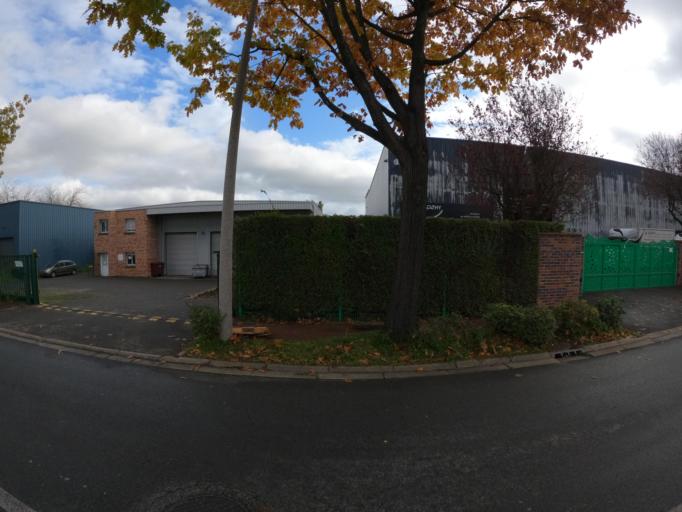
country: FR
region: Ile-de-France
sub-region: Departement de Seine-et-Marne
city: Chelles
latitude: 48.8909
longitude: 2.5977
